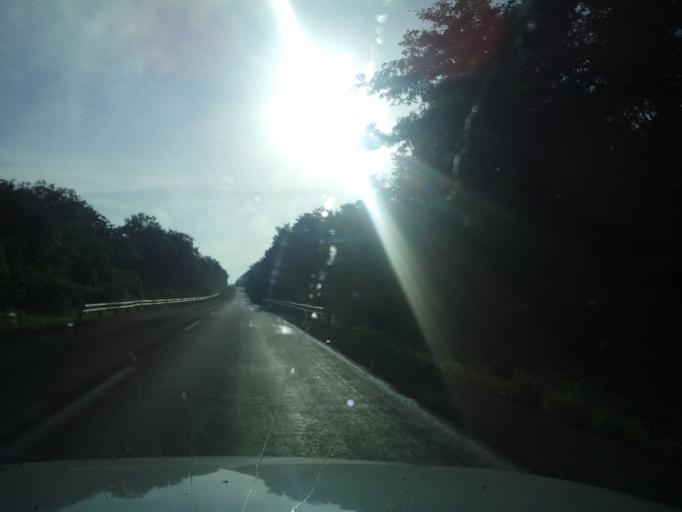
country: MX
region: Yucatan
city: Piste
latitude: 20.7495
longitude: -88.7175
